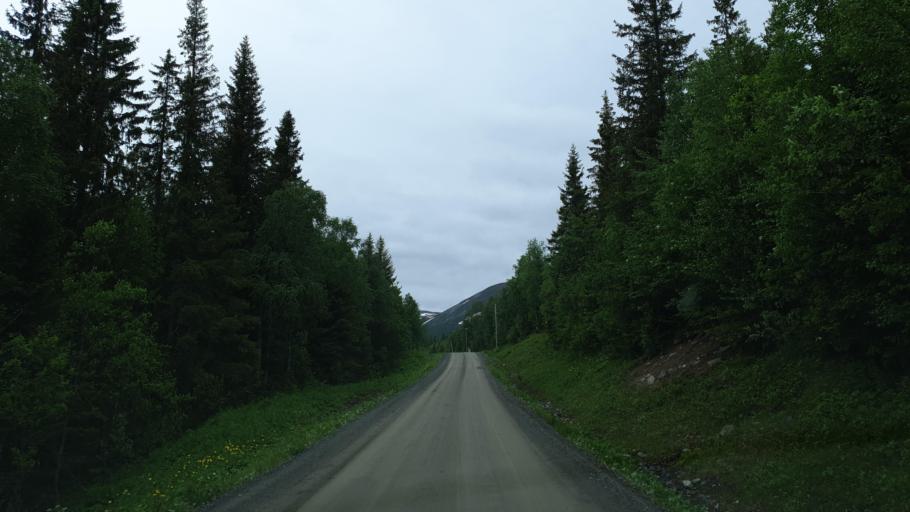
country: SE
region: Vaesterbotten
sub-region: Vilhelmina Kommun
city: Sjoberg
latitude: 65.3499
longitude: 15.8513
